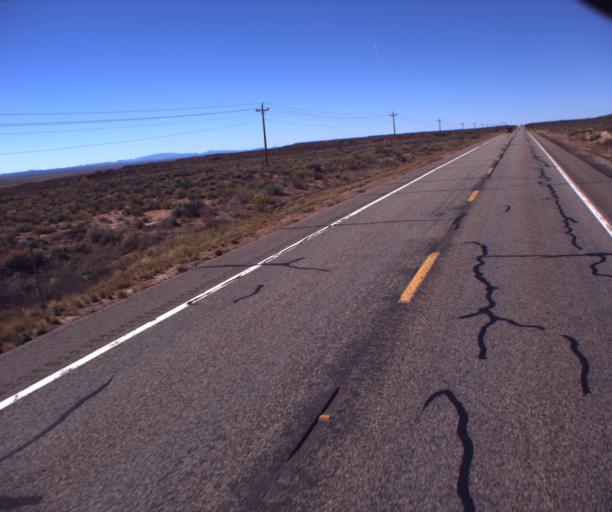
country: US
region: Arizona
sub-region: Coconino County
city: Fredonia
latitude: 36.8766
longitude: -112.6579
